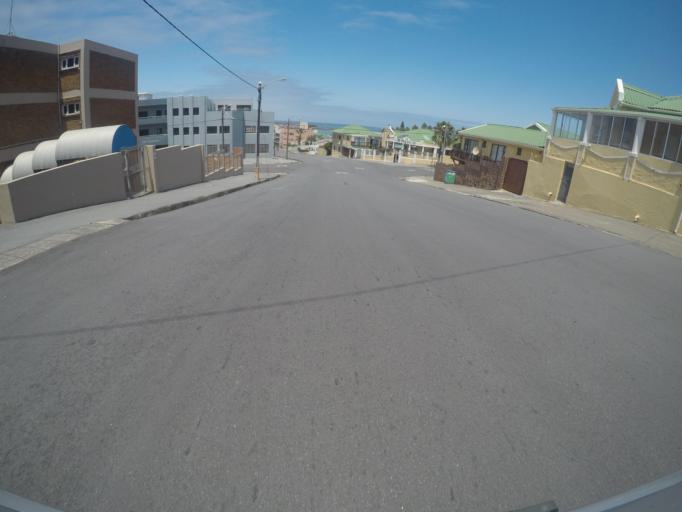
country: ZA
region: Eastern Cape
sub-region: Buffalo City Metropolitan Municipality
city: East London
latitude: -33.0182
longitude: 27.9169
